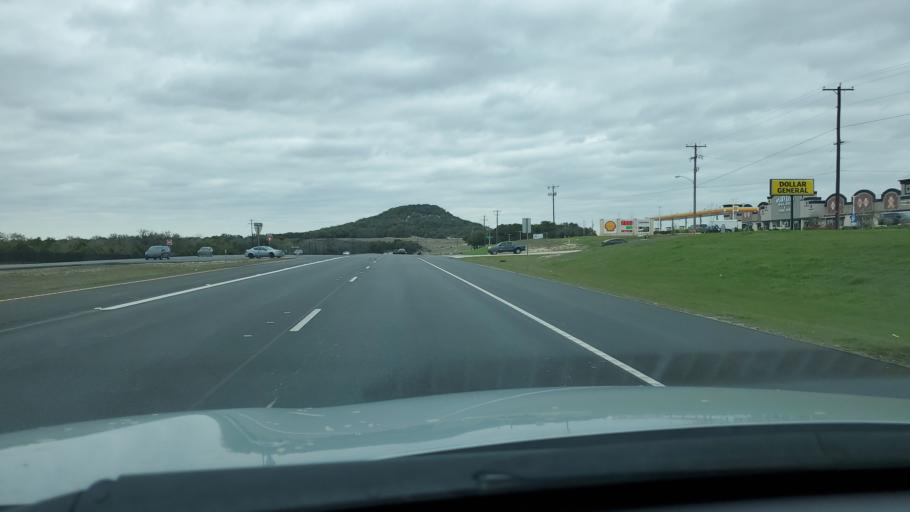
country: US
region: Texas
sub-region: Bell County
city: Killeen
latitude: 31.0337
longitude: -97.7587
